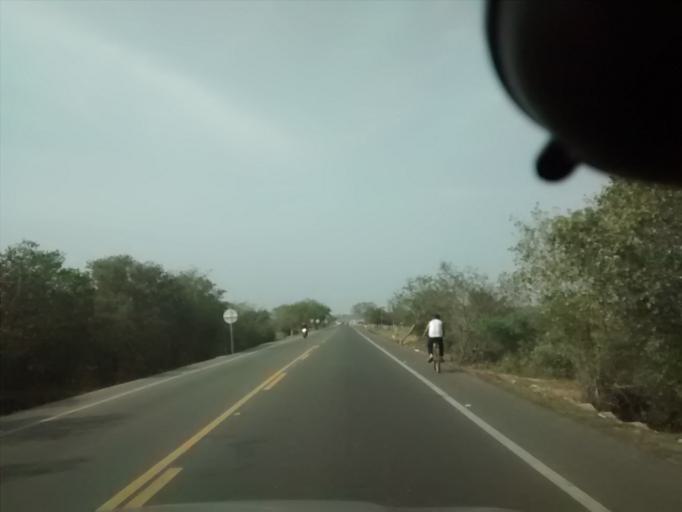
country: CO
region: Bolivar
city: Cartagena
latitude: 10.4939
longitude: -75.4804
